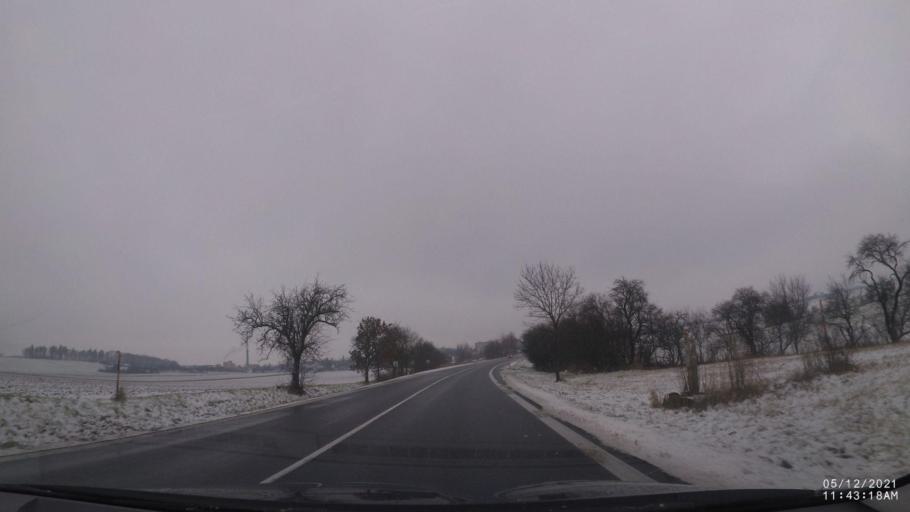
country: CZ
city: Dobruska
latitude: 50.2850
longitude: 16.1734
